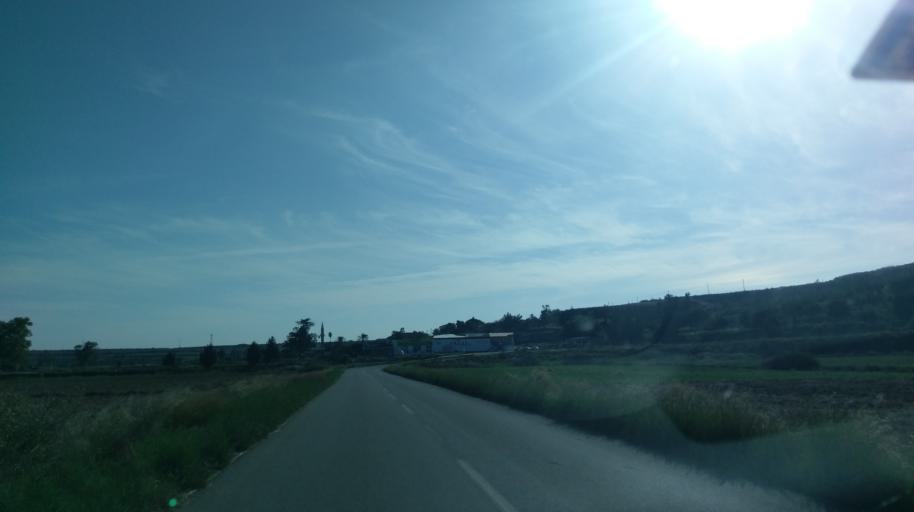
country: CY
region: Ammochostos
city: Trikomo
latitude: 35.2782
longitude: 33.8525
